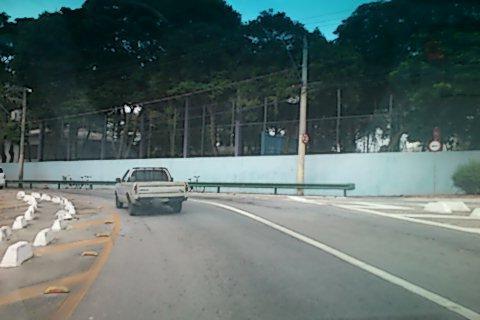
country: BR
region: Sao Paulo
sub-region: Sao Jose Dos Campos
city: Sao Jose dos Campos
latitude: -23.2092
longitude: -45.8854
